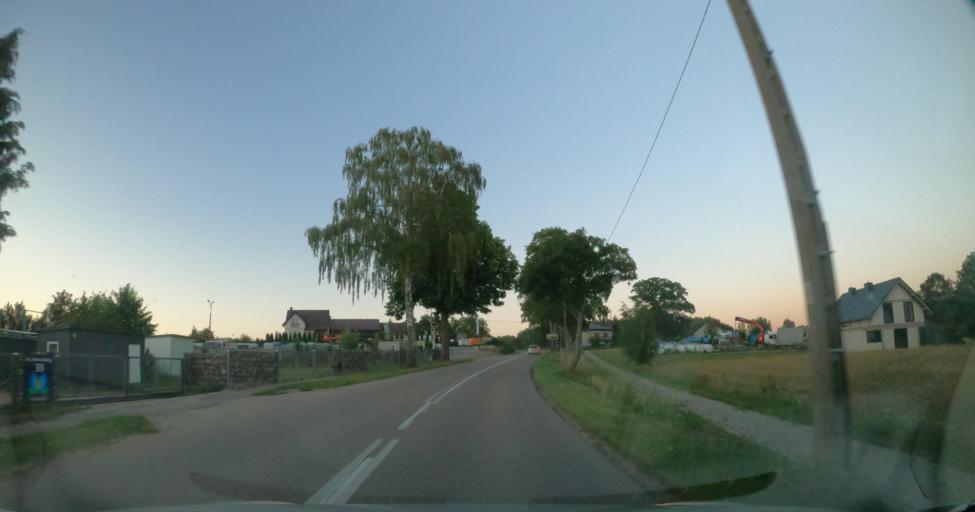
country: PL
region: Pomeranian Voivodeship
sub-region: Powiat wejherowski
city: Linia
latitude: 54.4549
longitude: 18.0334
